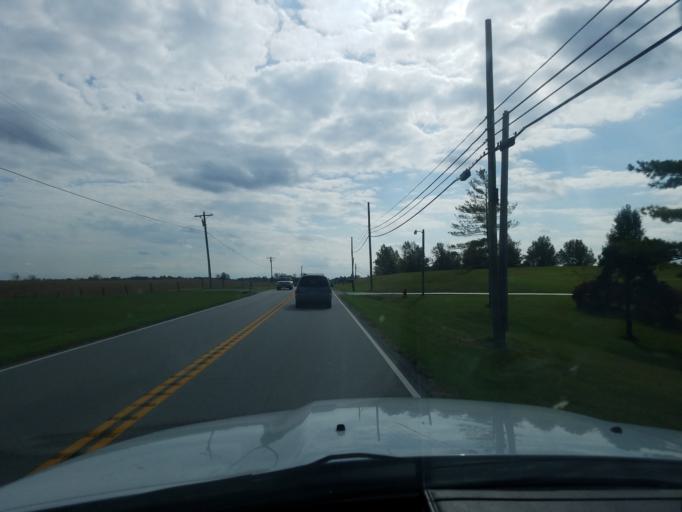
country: US
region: Kentucky
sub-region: Nelson County
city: Bardstown
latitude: 37.8601
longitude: -85.4632
